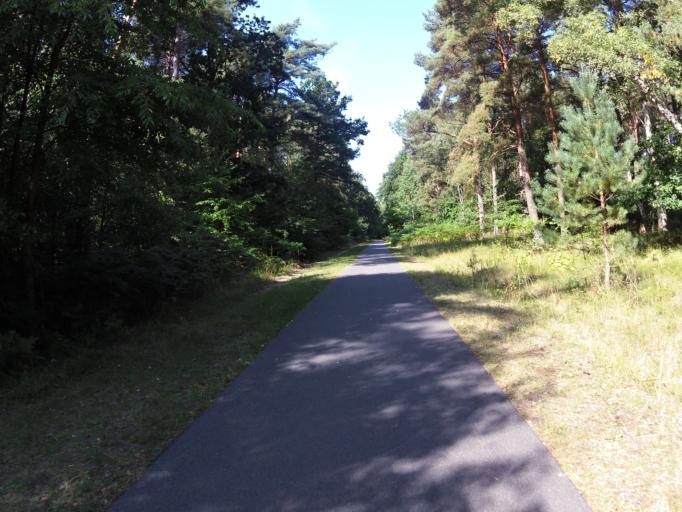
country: DE
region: Mecklenburg-Vorpommern
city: Karlshagen
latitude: 54.1373
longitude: 13.8155
